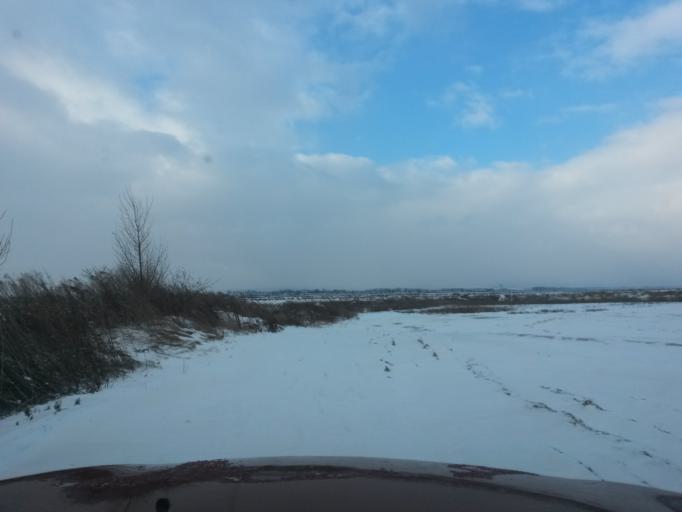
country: SK
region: Kosicky
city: Kosice
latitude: 48.6290
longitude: 21.3381
